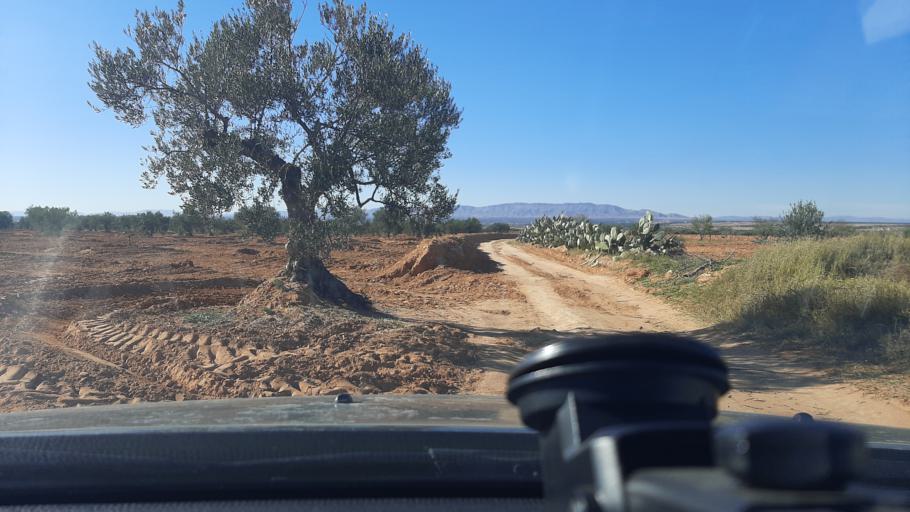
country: TN
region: Safaqis
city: Bi'r `Ali Bin Khalifah
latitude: 34.9993
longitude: 10.0894
